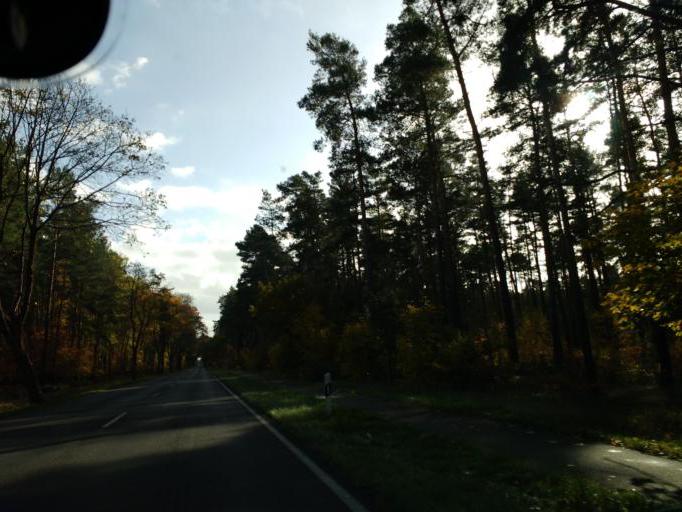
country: DE
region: Brandenburg
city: Grunheide
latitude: 52.3778
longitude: 13.8331
